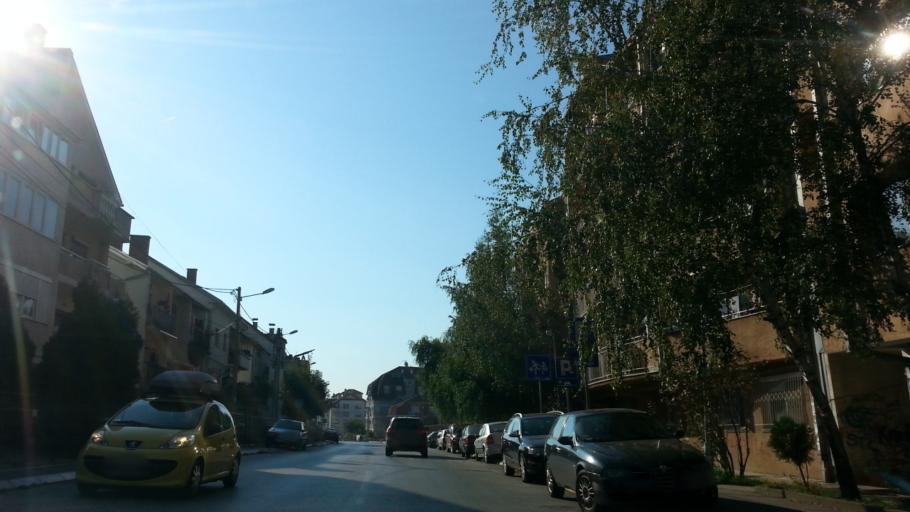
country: RS
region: Central Serbia
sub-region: Belgrade
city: Cukarica
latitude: 44.7597
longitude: 20.4197
